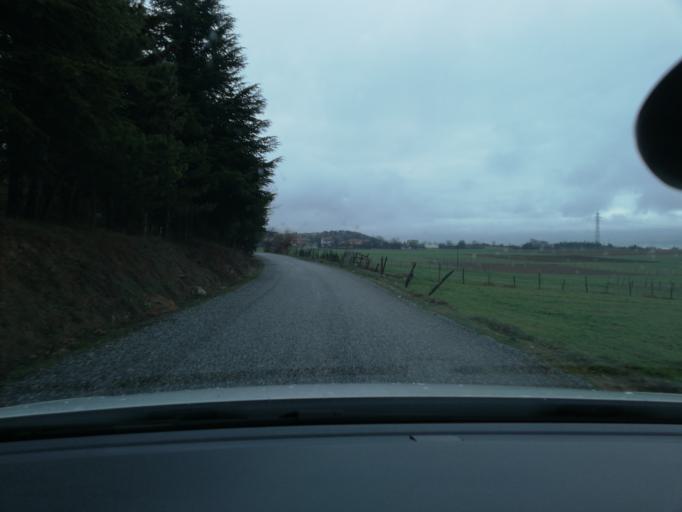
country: TR
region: Bolu
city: Bolu
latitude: 40.7722
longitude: 31.6515
